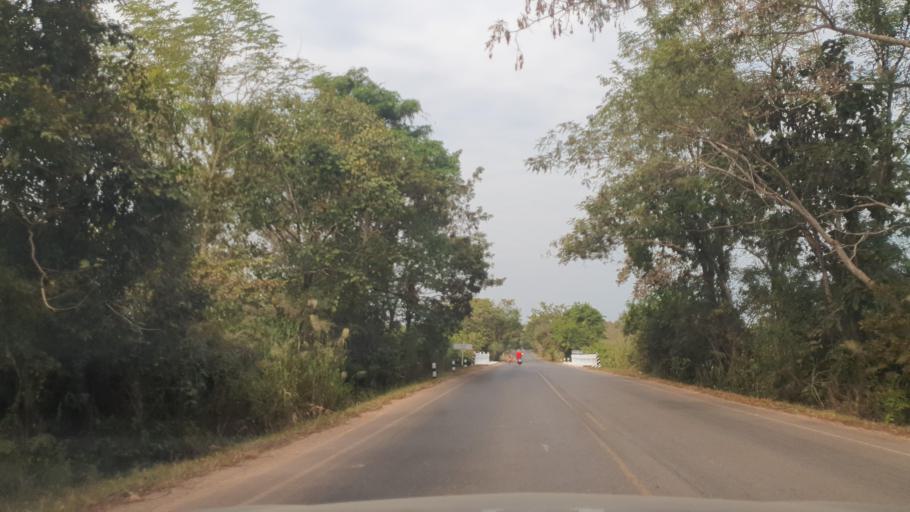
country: TH
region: Changwat Bueng Kan
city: Bung Khla
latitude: 18.2229
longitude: 104.0360
